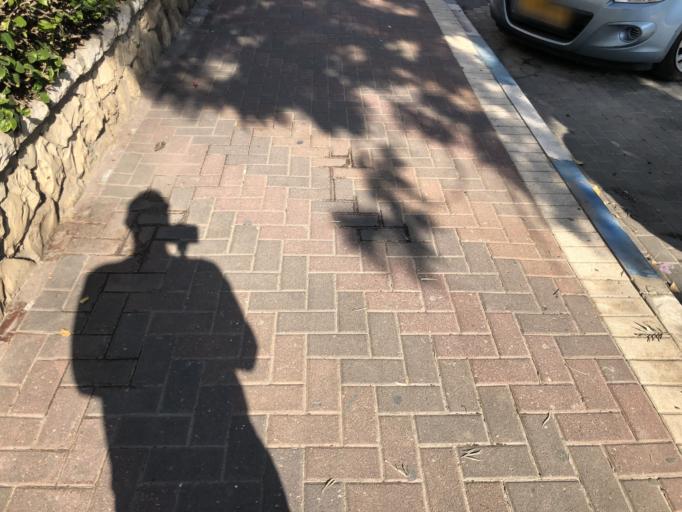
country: IL
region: Tel Aviv
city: Giv`atayim
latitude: 32.0725
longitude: 34.8123
